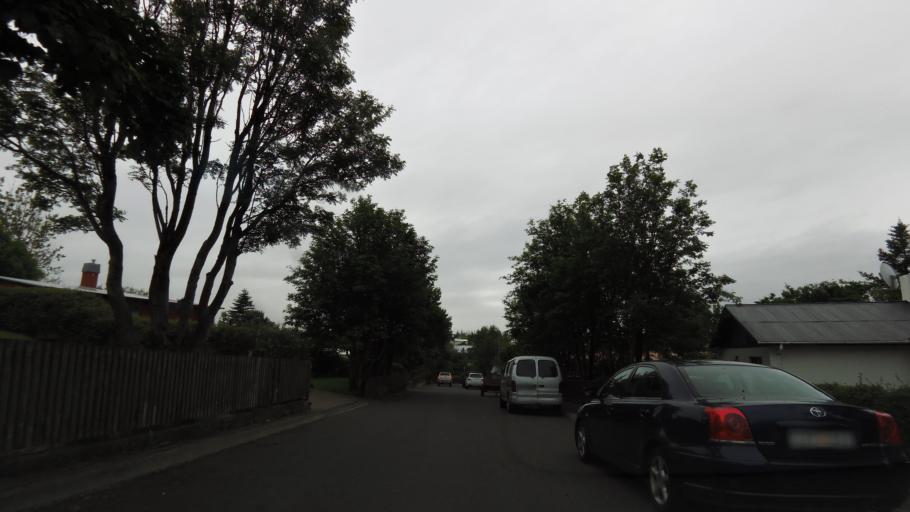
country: IS
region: Capital Region
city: Kopavogur
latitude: 64.1071
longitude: -21.9036
